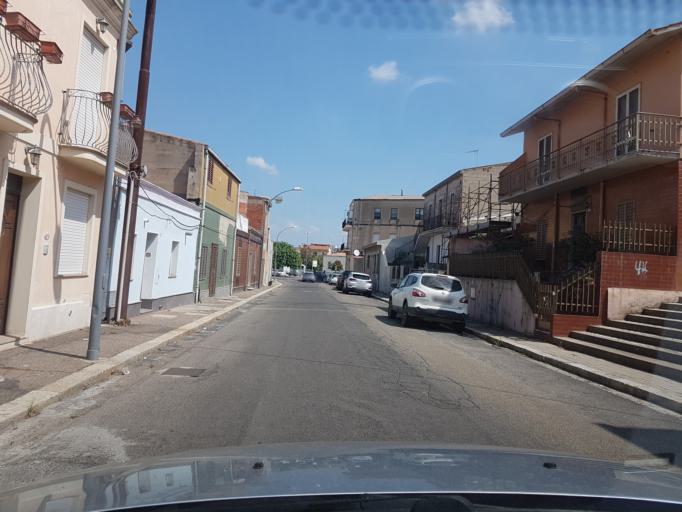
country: IT
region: Sardinia
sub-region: Provincia di Oristano
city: Oristano
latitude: 39.9059
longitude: 8.5995
